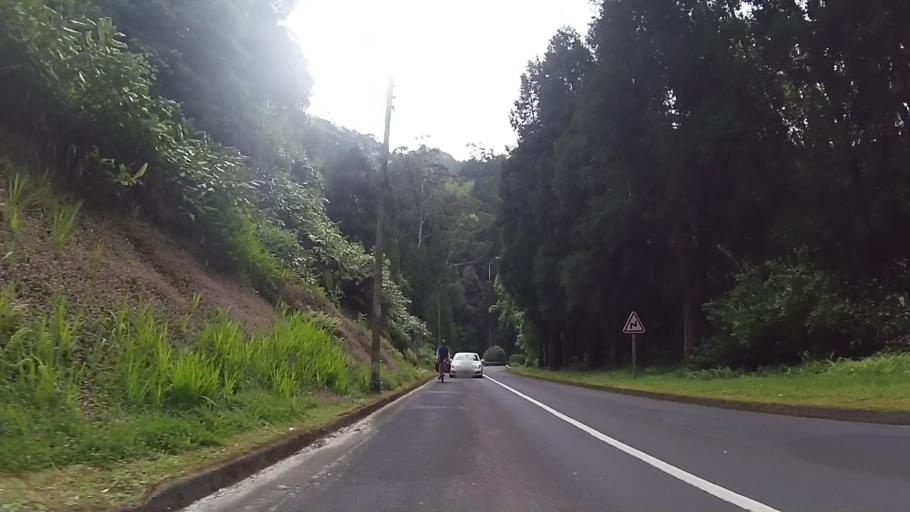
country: PT
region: Azores
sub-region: Povoacao
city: Furnas
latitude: 37.7638
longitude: -25.2868
